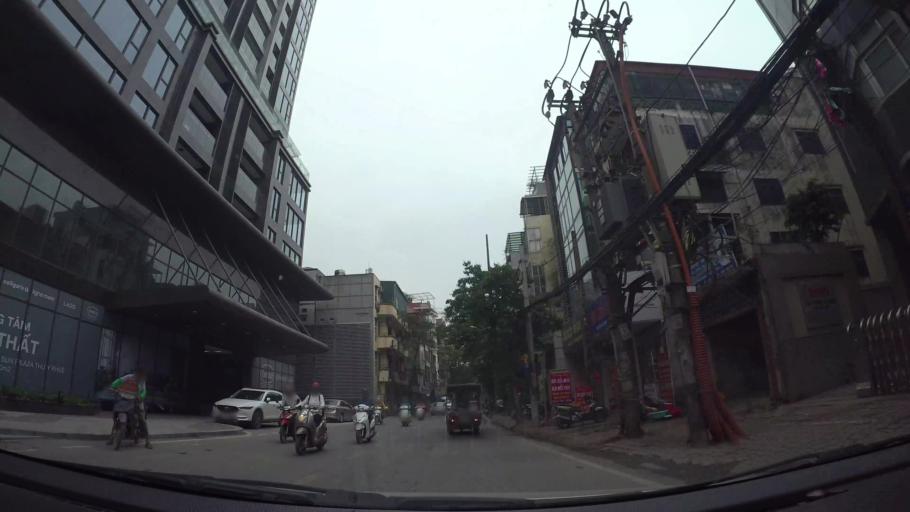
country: VN
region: Ha Noi
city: Dong Da
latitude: 21.0415
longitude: 105.8266
